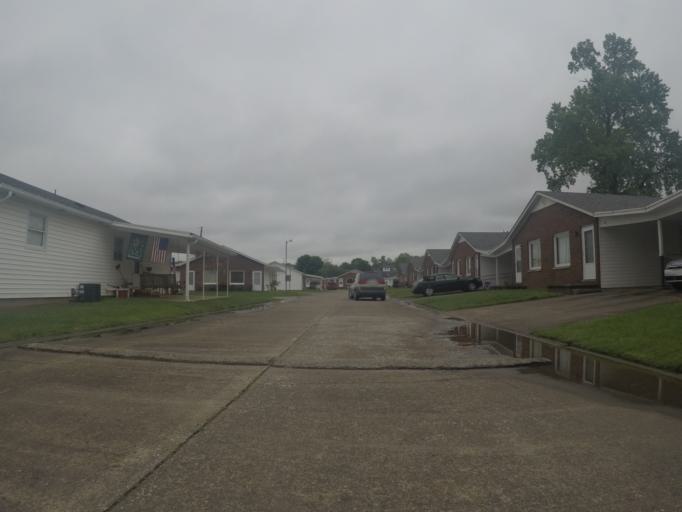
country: US
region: West Virginia
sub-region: Cabell County
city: Barboursville
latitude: 38.4128
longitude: -82.3006
